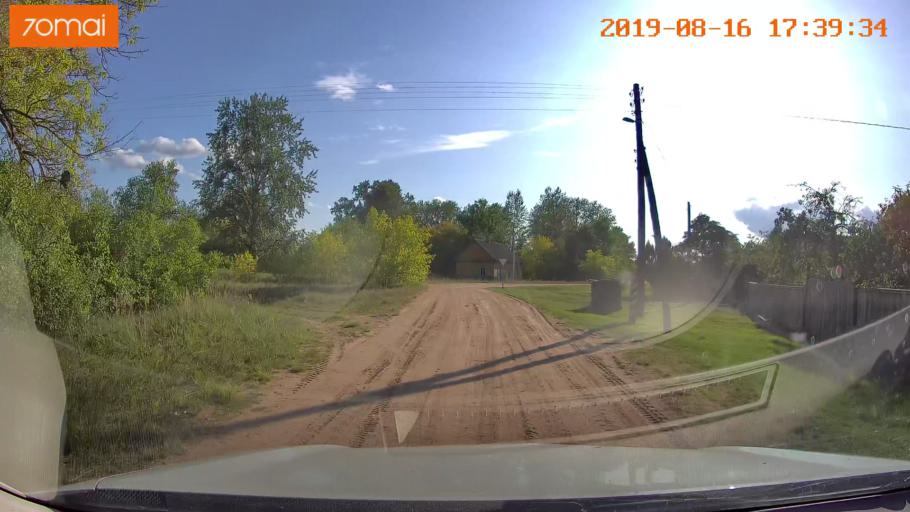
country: BY
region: Mogilev
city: Asipovichy
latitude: 53.2449
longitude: 28.6871
